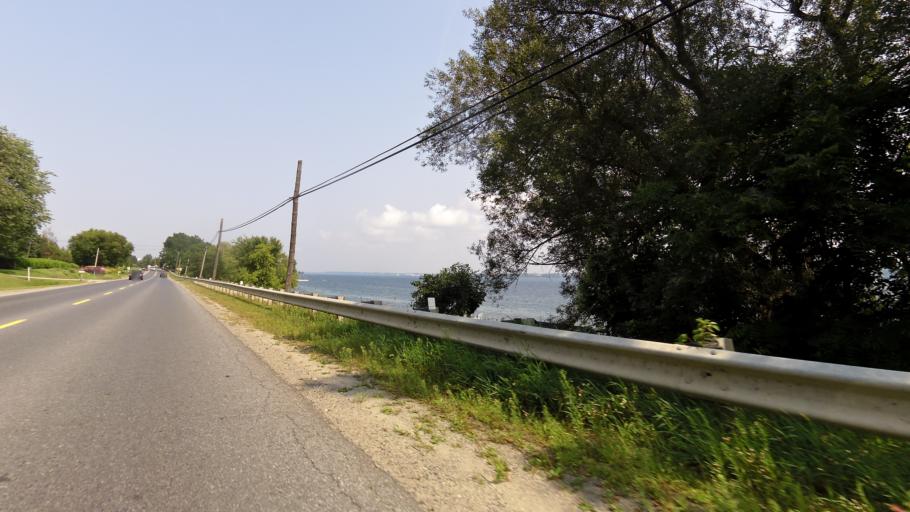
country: CA
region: Ontario
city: Prescott
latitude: 44.6943
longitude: -75.5424
